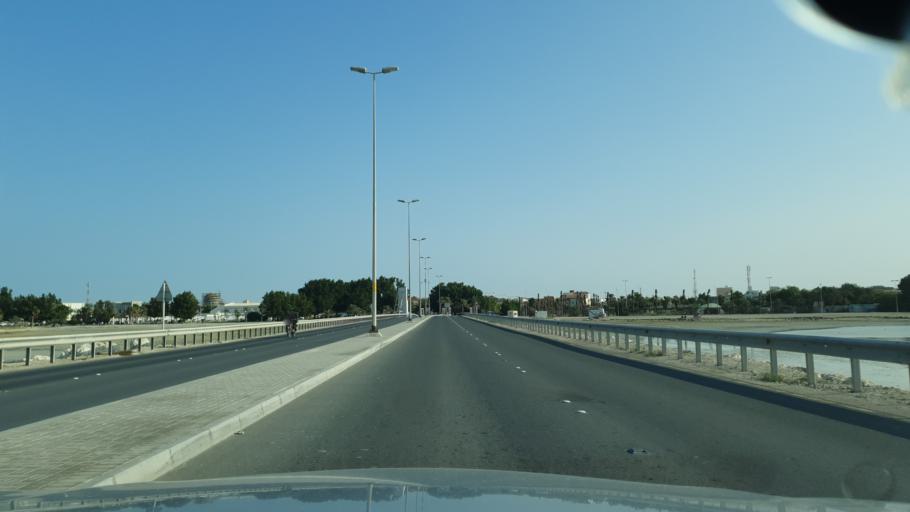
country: BH
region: Manama
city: Jidd Hafs
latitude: 26.2261
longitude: 50.4576
